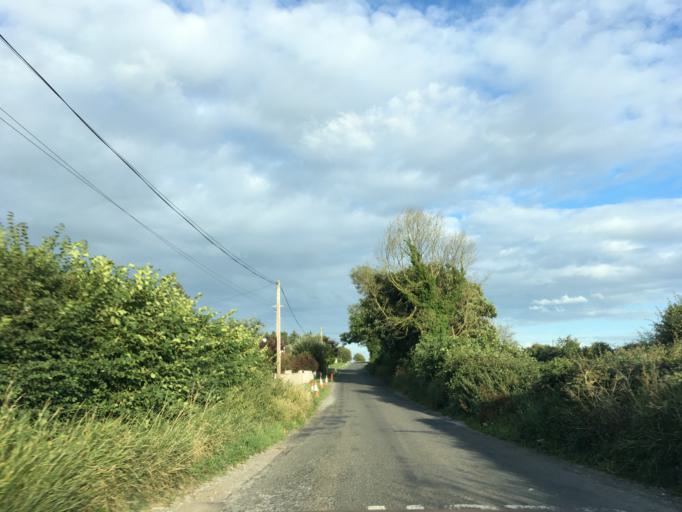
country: IE
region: Munster
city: Cashel
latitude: 52.4795
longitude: -7.8999
